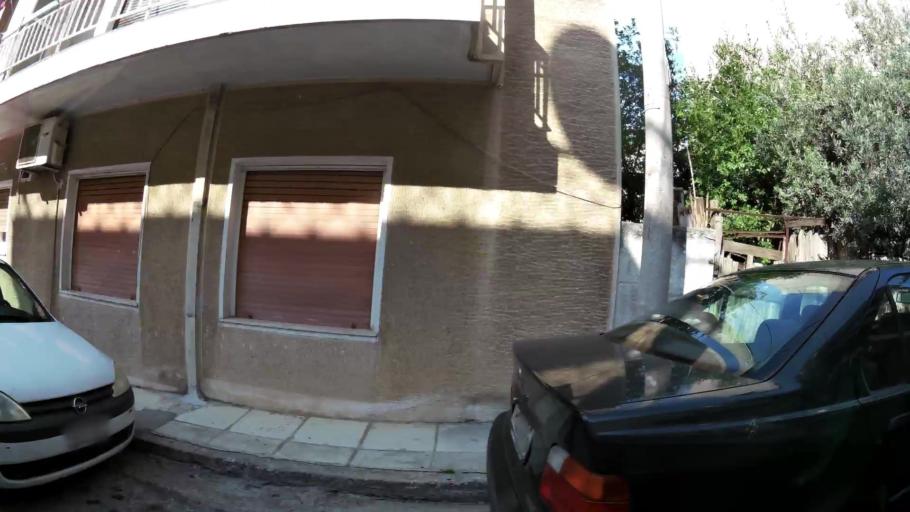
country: GR
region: Attica
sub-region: Nomarchia Athinas
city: Galatsi
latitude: 38.0152
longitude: 23.7470
